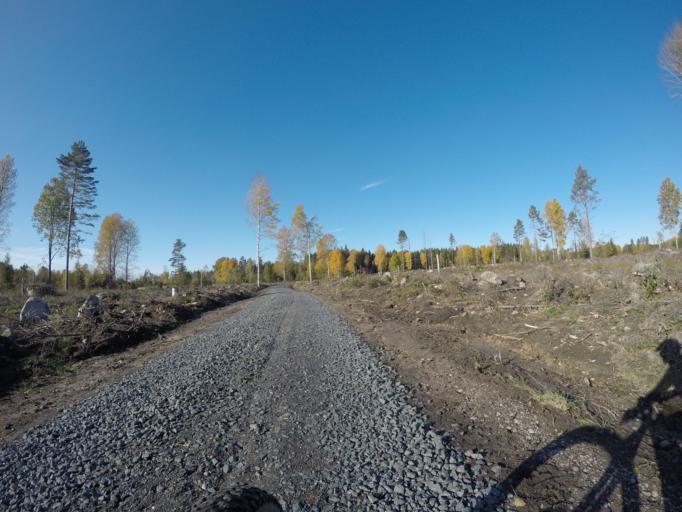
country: SE
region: Vaestmanland
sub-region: Kungsors Kommun
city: Kungsoer
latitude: 59.3275
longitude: 16.1034
